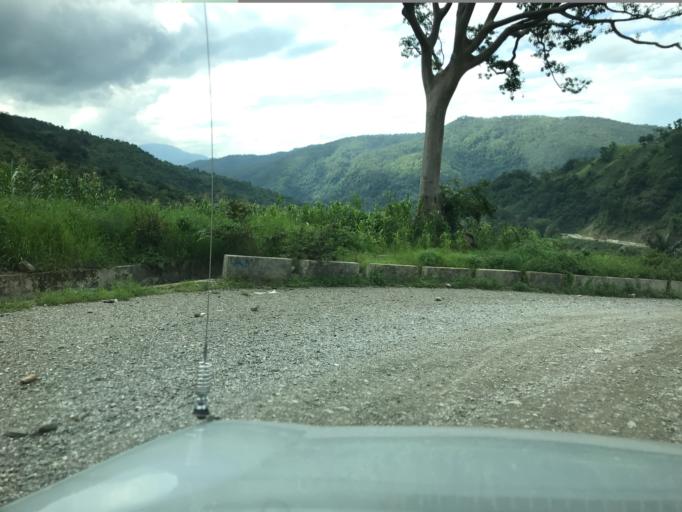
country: TL
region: Aileu
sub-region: Aileu Villa
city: Aileu
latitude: -8.6489
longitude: 125.5253
